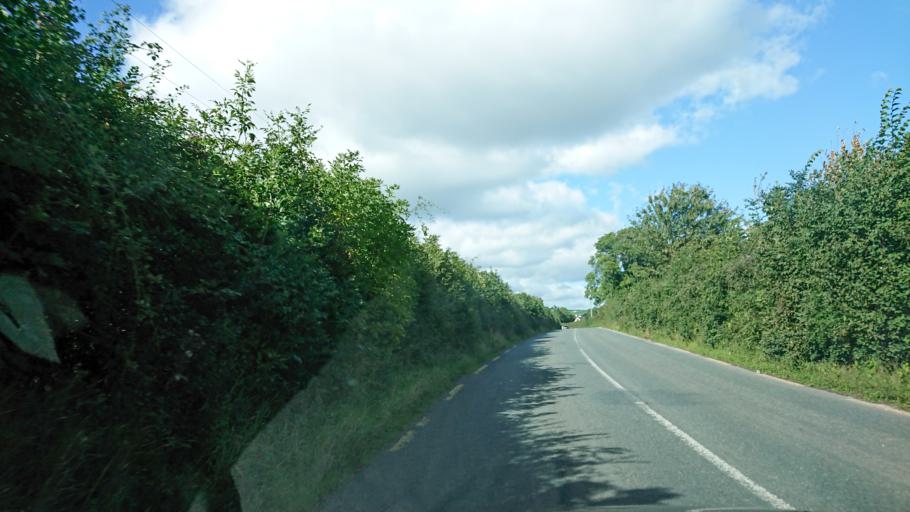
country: IE
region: Munster
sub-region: Waterford
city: Dungarvan
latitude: 52.1114
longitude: -7.6786
